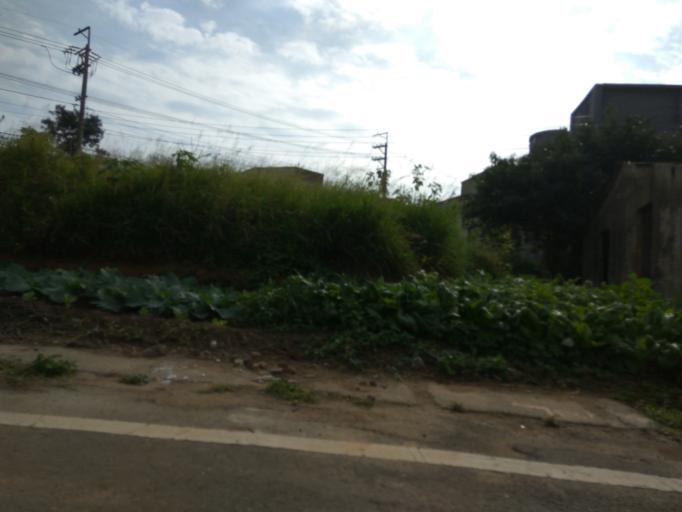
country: TW
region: Taiwan
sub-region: Hsinchu
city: Zhubei
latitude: 24.9762
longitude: 121.0266
